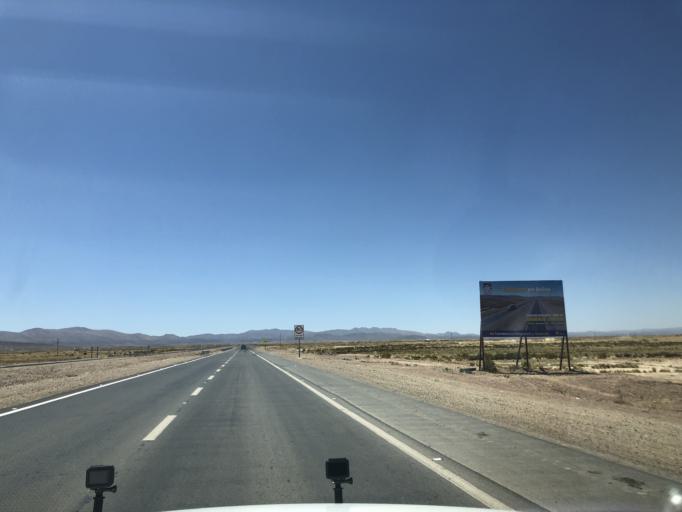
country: BO
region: La Paz
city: Colquiri
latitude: -17.6492
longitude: -67.2014
